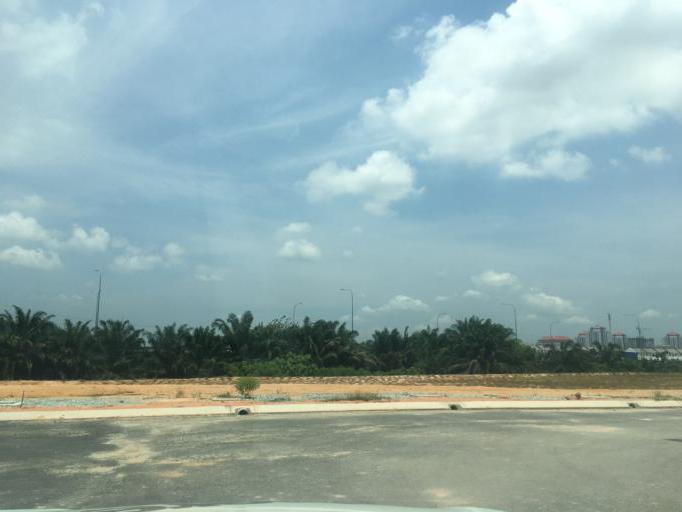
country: MY
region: Putrajaya
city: Putrajaya
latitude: 2.8447
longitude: 101.7111
